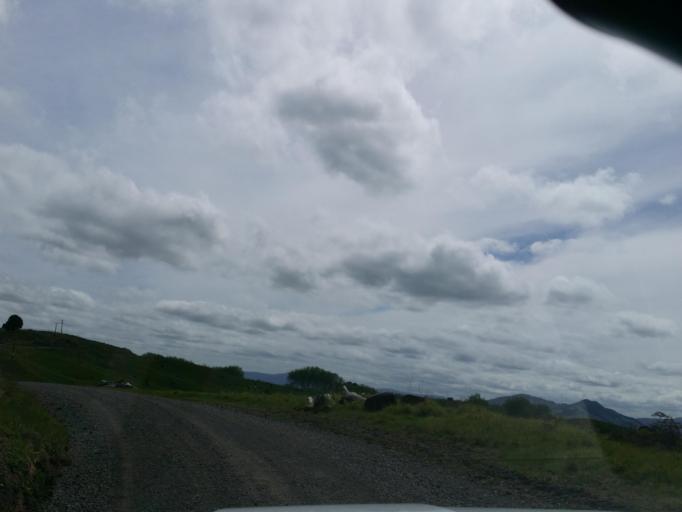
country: NZ
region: Northland
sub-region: Kaipara District
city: Dargaville
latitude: -35.9106
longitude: 174.0363
